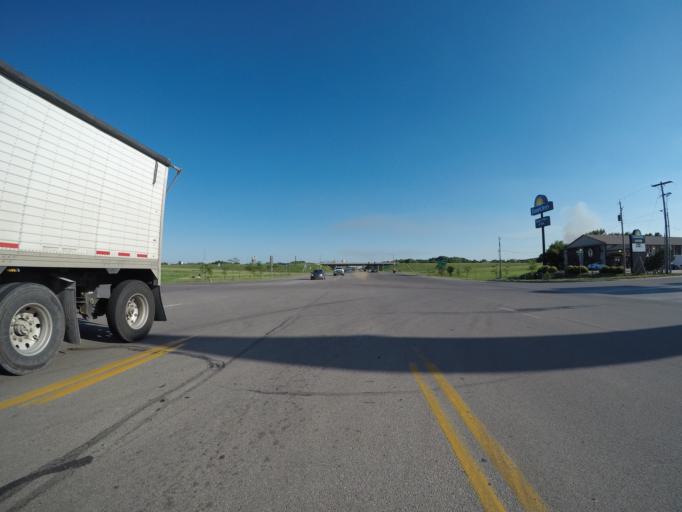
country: US
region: Kansas
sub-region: Saline County
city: Salina
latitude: 38.8787
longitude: -97.6123
